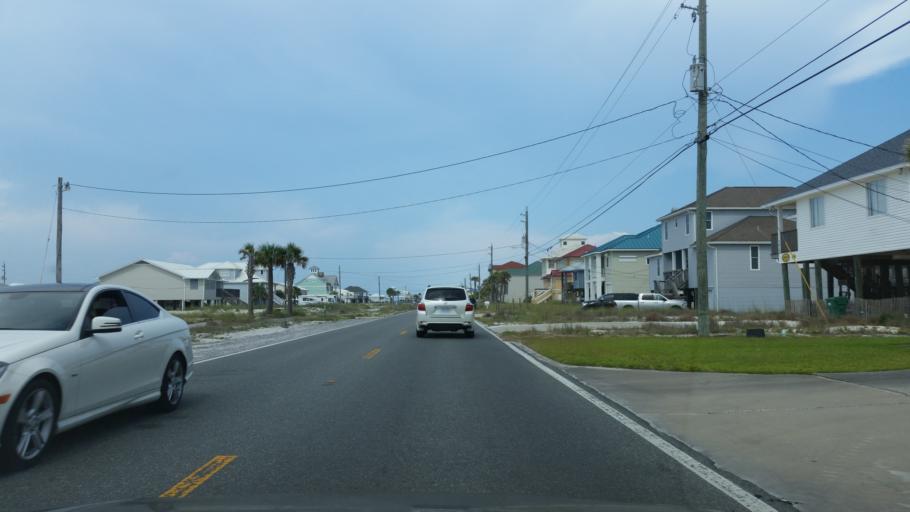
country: US
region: Florida
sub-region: Santa Rosa County
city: Navarre
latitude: 30.3739
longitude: -86.9058
